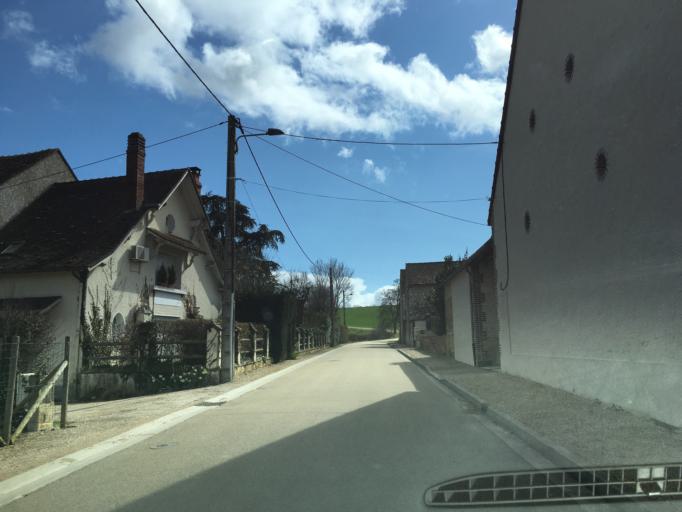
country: FR
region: Bourgogne
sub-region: Departement de l'Yonne
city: Pourrain
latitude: 47.7817
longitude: 3.4068
